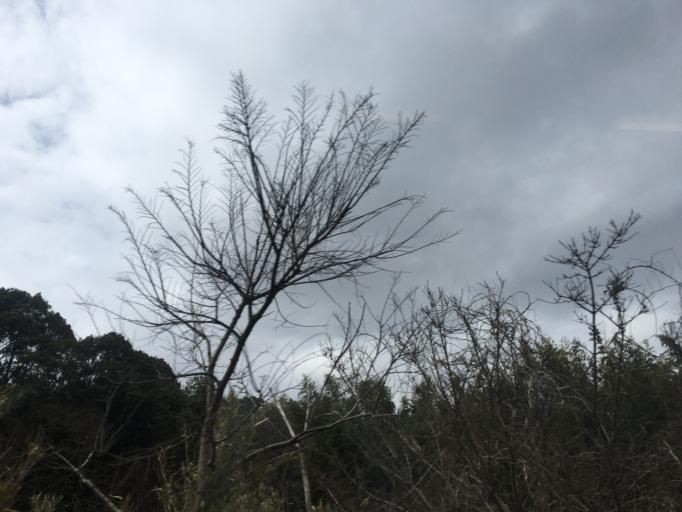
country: JP
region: Chiba
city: Shisui
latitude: 35.7463
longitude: 140.2910
